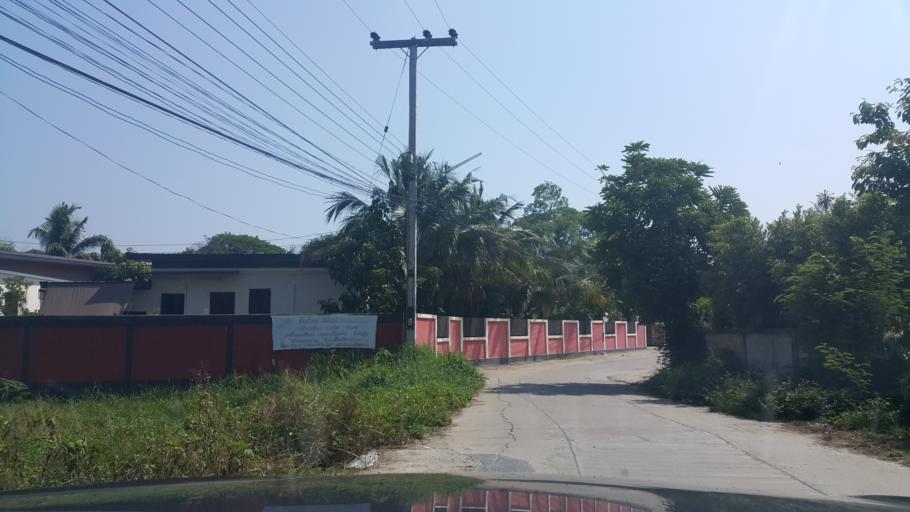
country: TH
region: Chiang Mai
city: Saraphi
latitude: 18.7242
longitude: 98.9740
